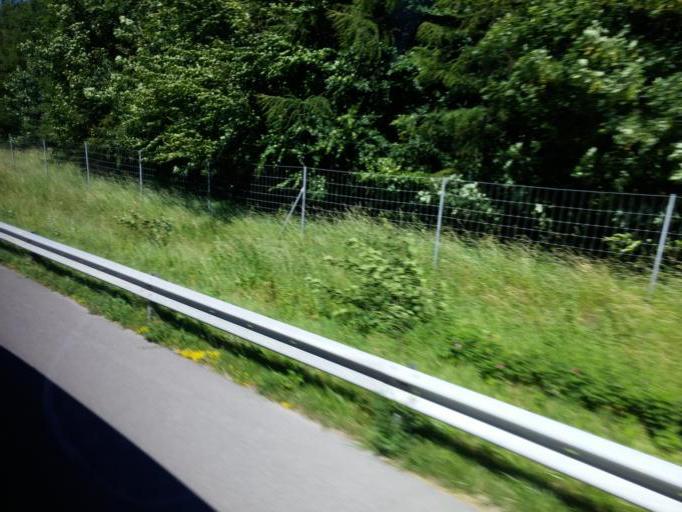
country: SE
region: Skane
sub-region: Malmo
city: Oxie
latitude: 55.5456
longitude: 13.1456
